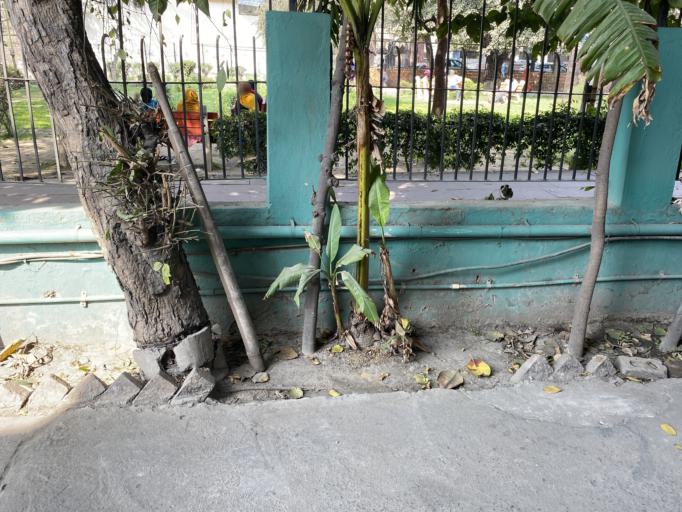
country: IN
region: NCT
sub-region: North West Delhi
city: Pitampura
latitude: 28.6917
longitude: 77.1014
